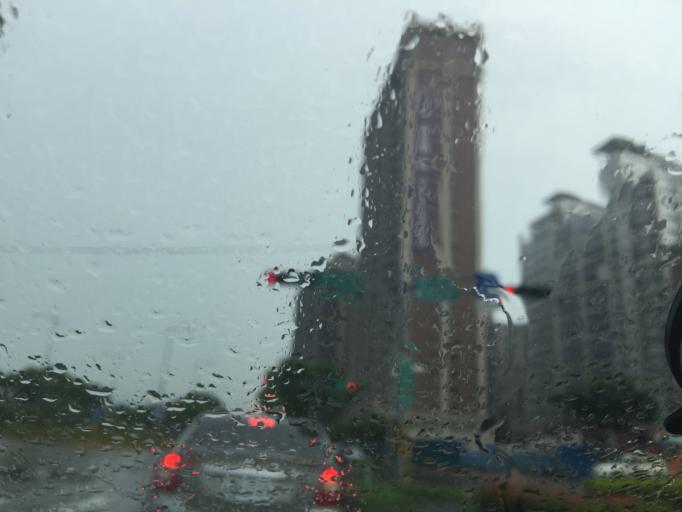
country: TW
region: Taiwan
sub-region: Hsinchu
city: Zhubei
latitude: 24.8117
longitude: 121.0370
